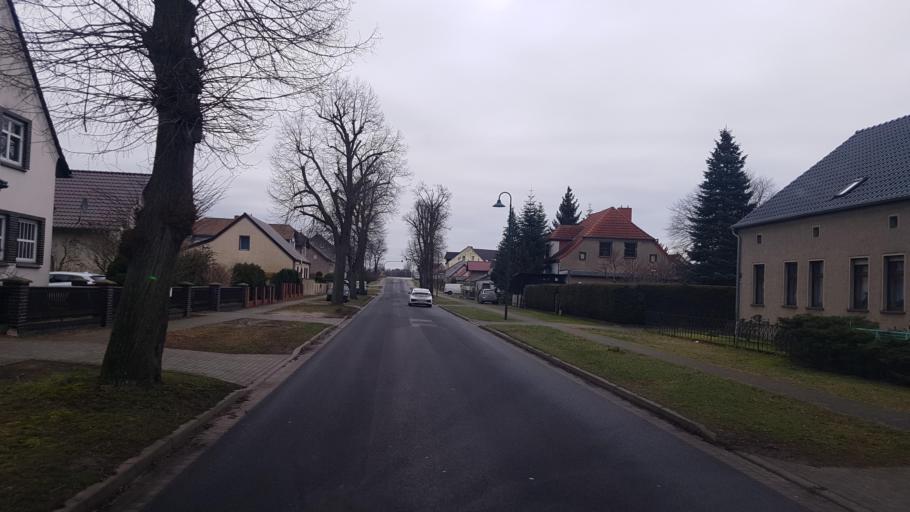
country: DE
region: Brandenburg
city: Oranienburg
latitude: 52.8688
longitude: 13.2085
